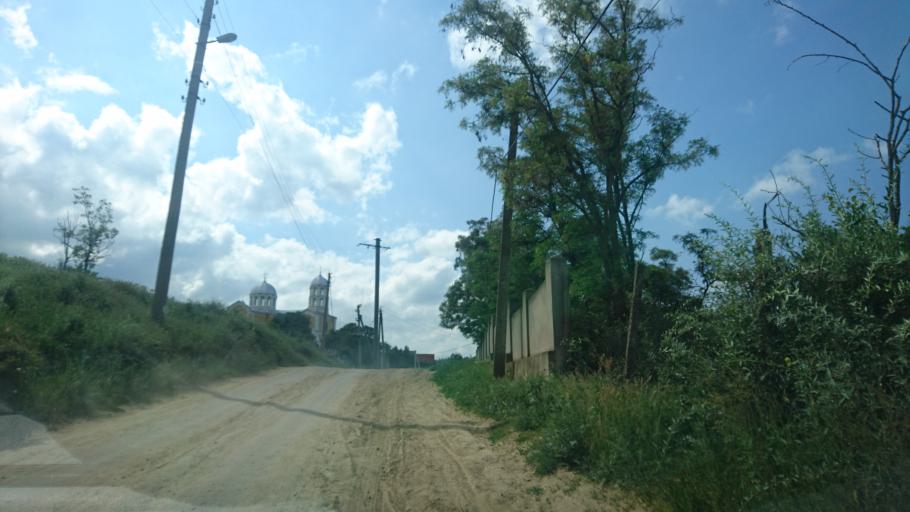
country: MD
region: Telenesti
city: Cocieri
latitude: 47.3578
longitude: 29.1058
